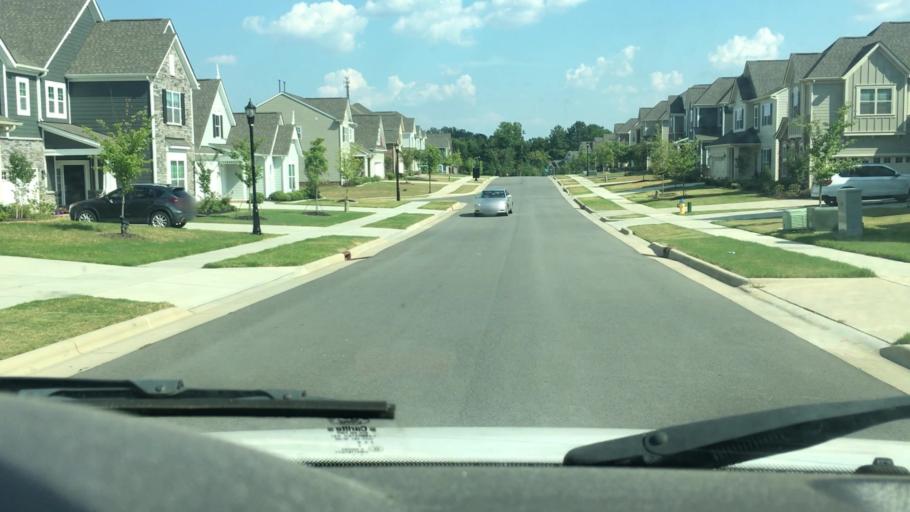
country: US
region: North Carolina
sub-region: Mecklenburg County
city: Huntersville
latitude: 35.4271
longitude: -80.7557
